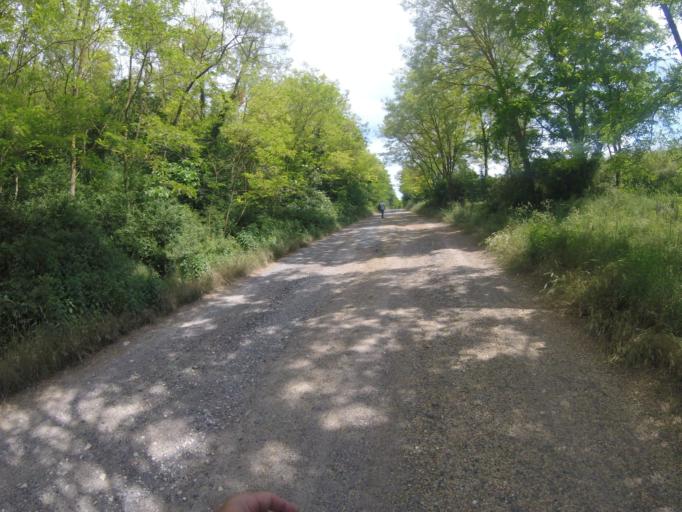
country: HU
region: Zala
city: Zalaszentgrot
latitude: 46.8902
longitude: 17.0591
